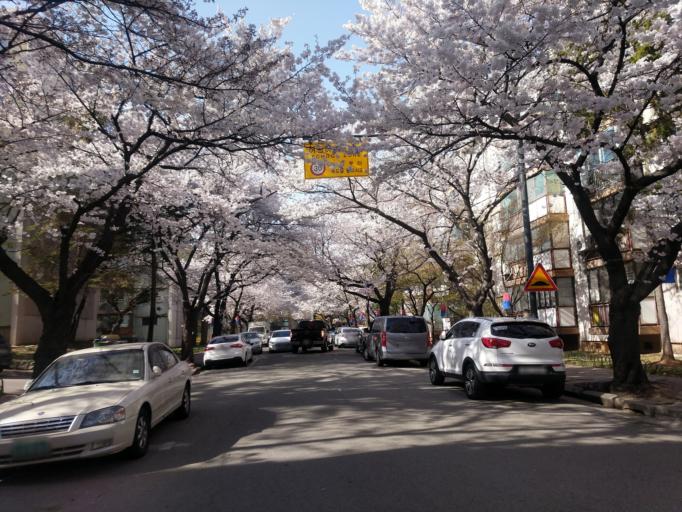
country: KR
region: Gyeonggi-do
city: Kwangmyong
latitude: 37.4814
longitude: 126.8677
